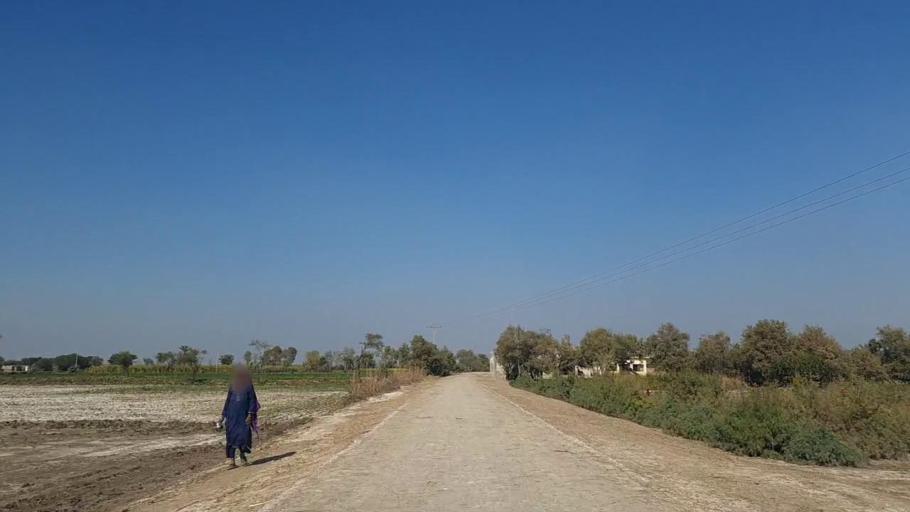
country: PK
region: Sindh
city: Bandhi
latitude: 26.5461
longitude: 68.3270
